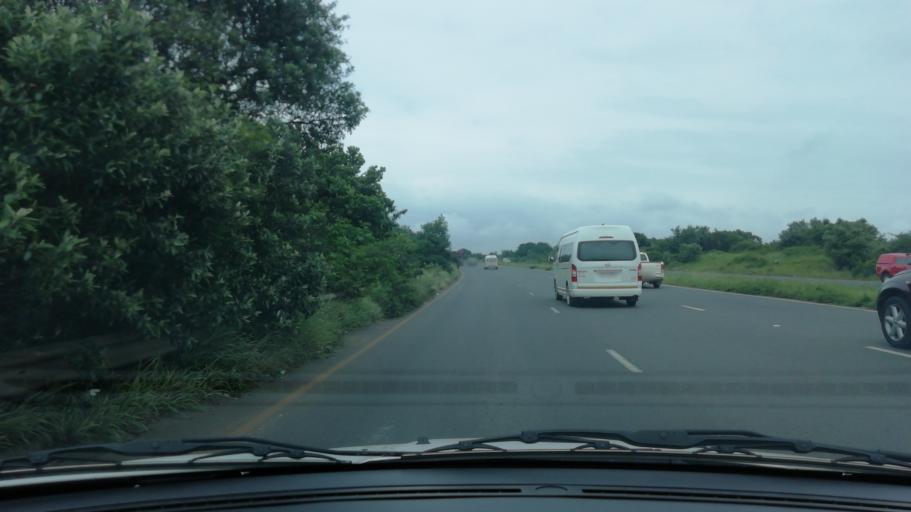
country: ZA
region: KwaZulu-Natal
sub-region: uThungulu District Municipality
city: Richards Bay
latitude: -28.7731
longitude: 32.0114
